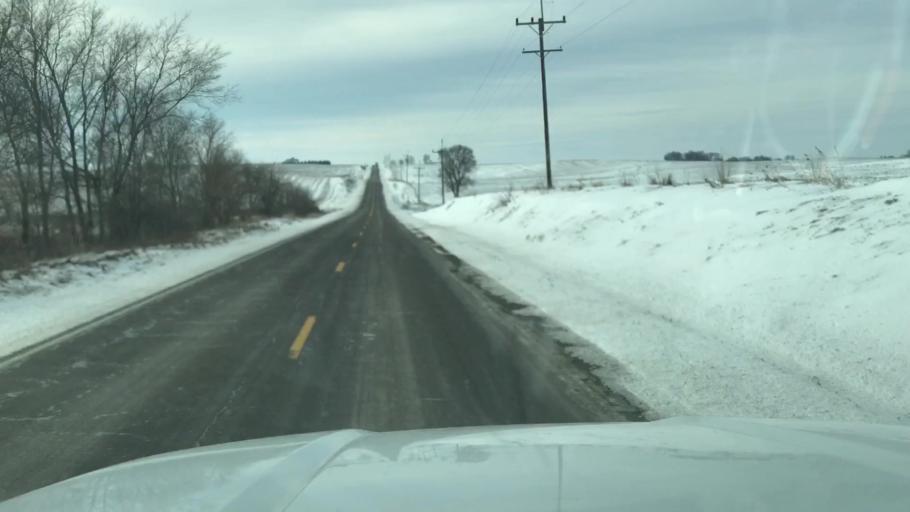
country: US
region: Missouri
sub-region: Holt County
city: Mound City
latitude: 40.1122
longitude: -95.1449
